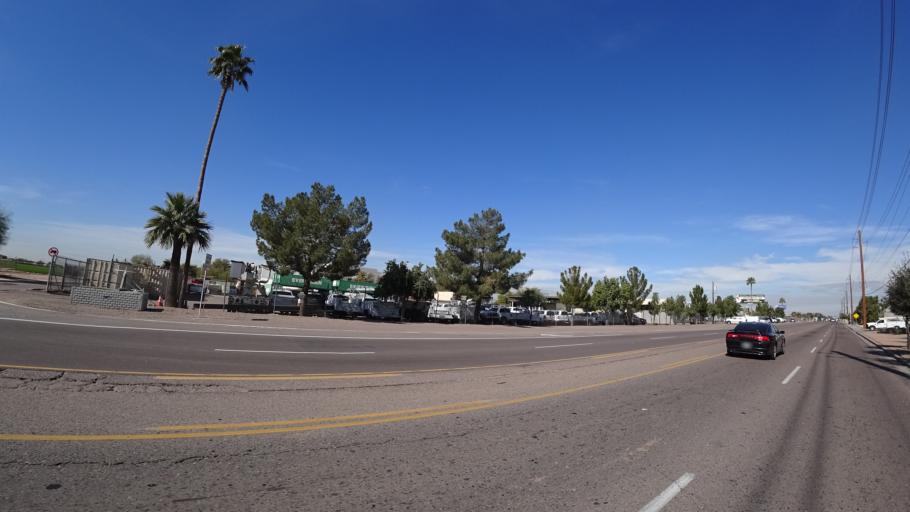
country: US
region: Arizona
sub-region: Maricopa County
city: Tolleson
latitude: 33.4319
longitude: -112.2038
